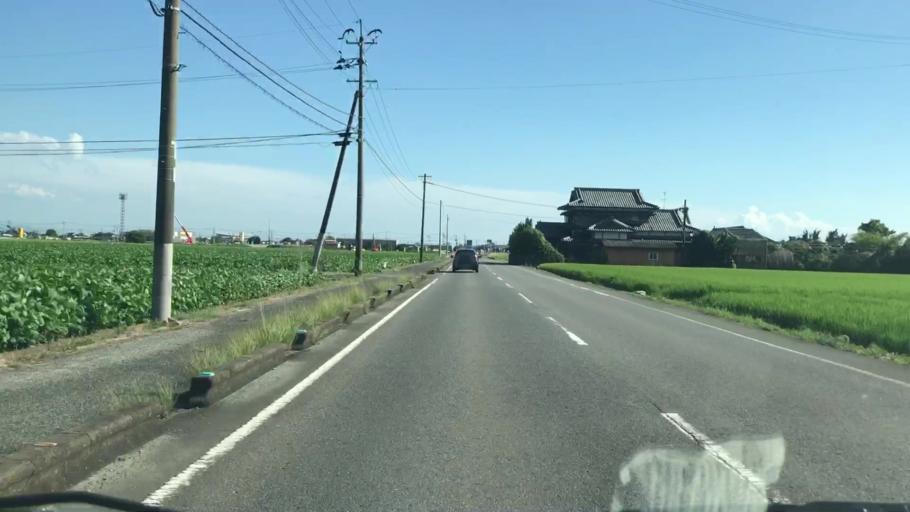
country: JP
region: Saga Prefecture
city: Okawa
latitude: 33.2180
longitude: 130.3346
